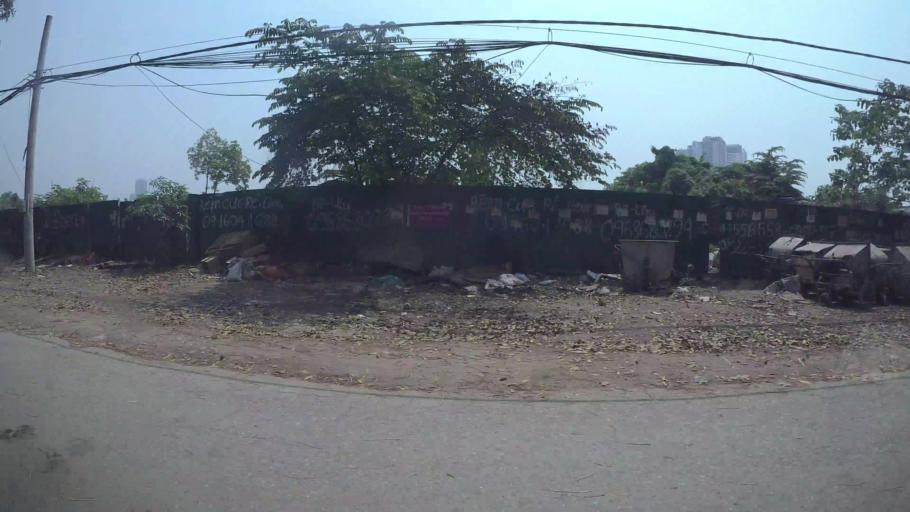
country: VN
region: Ha Noi
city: Ha Dong
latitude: 20.9928
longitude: 105.7616
